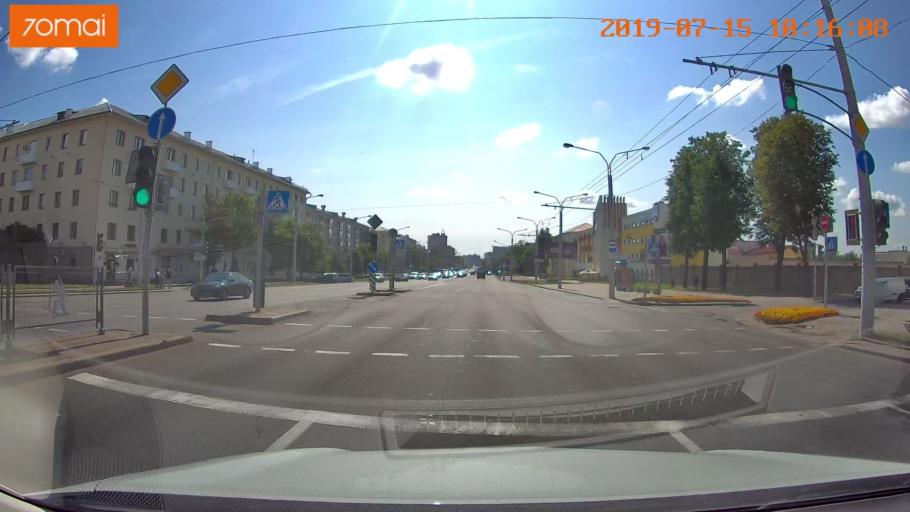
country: BY
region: Minsk
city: Minsk
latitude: 53.8857
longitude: 27.5846
